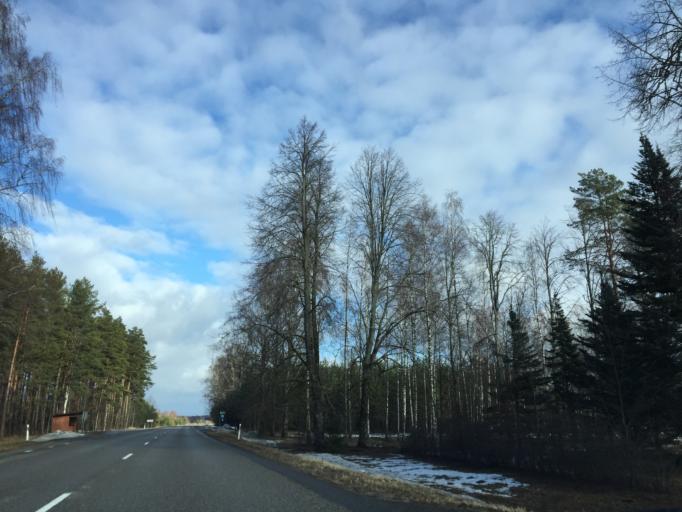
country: LV
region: Salacgrivas
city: Ainazi
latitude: 57.8606
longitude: 24.5381
